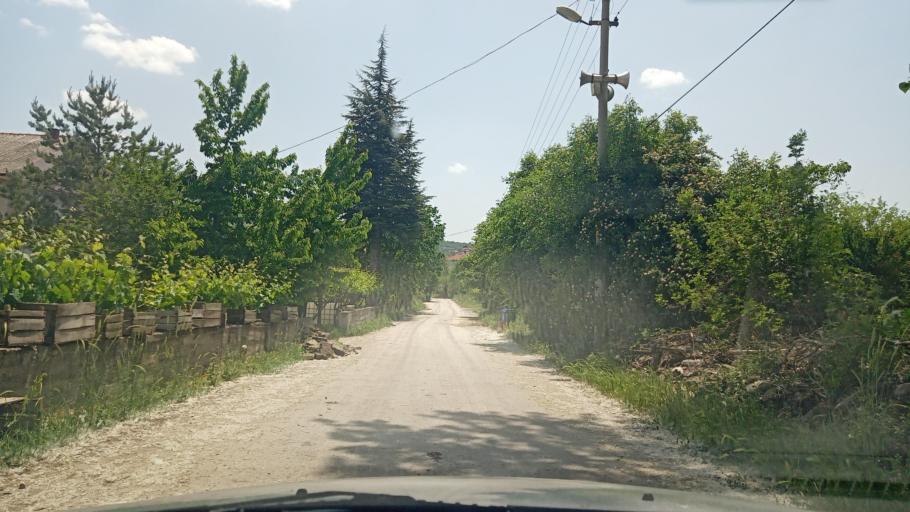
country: TR
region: Bolu
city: Seben
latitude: 40.4106
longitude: 31.5782
